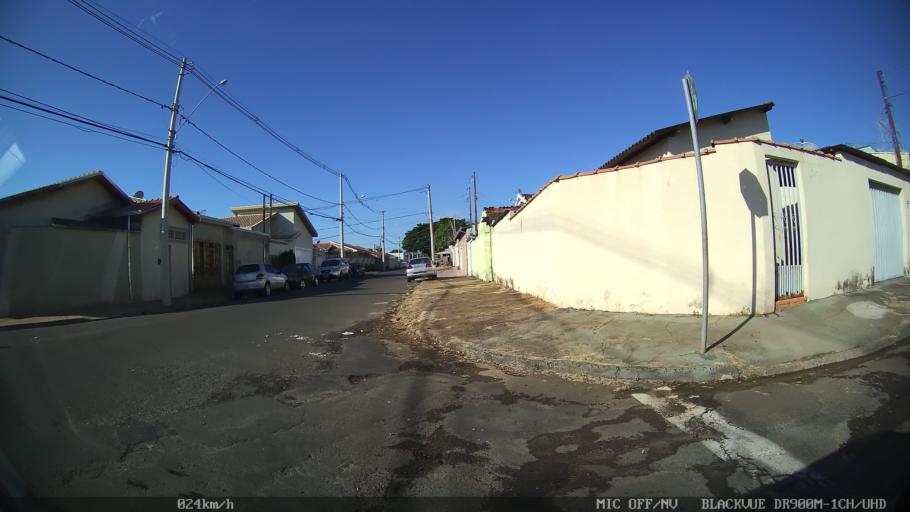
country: BR
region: Sao Paulo
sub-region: Franca
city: Franca
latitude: -20.5141
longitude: -47.4115
